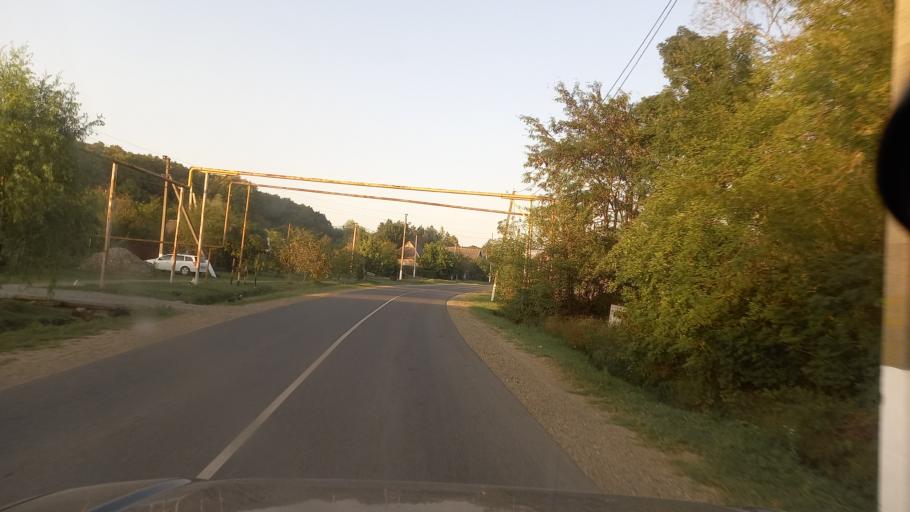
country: RU
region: Krasnodarskiy
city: Smolenskaya
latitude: 44.7676
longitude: 38.7795
